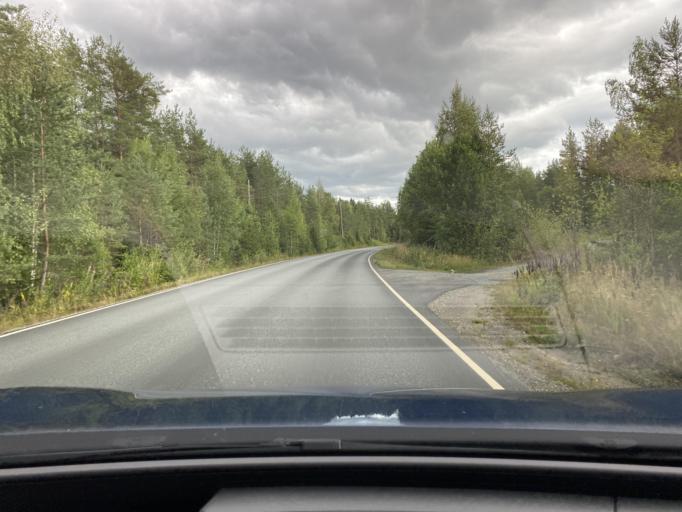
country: FI
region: Pirkanmaa
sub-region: Lounais-Pirkanmaa
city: Vammala
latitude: 61.3047
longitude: 22.9349
